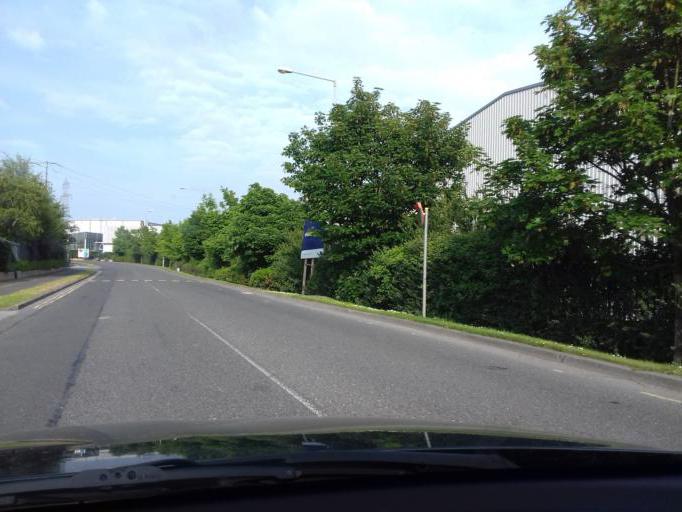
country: IE
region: Leinster
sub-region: Fingal County
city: Blanchardstown
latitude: 53.4106
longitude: -6.3504
